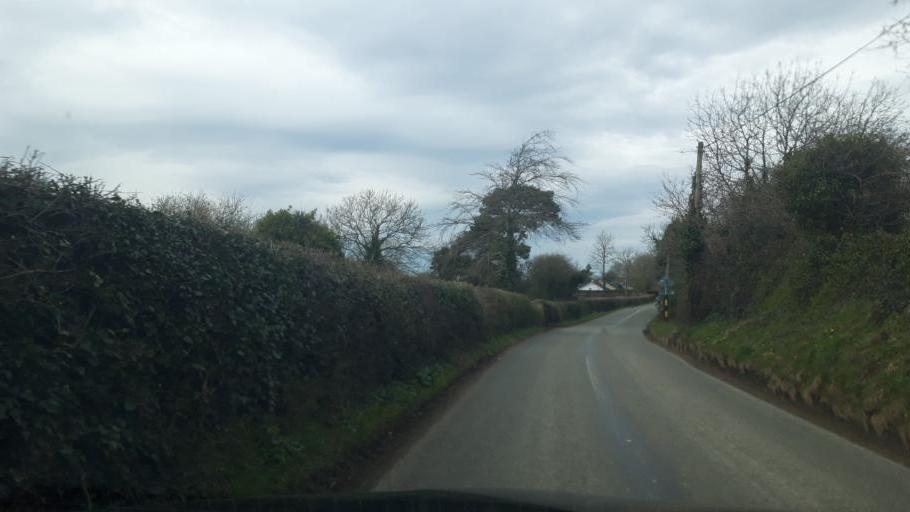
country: IE
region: Leinster
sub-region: Kildare
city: Rathangan
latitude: 53.2570
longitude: -6.9339
